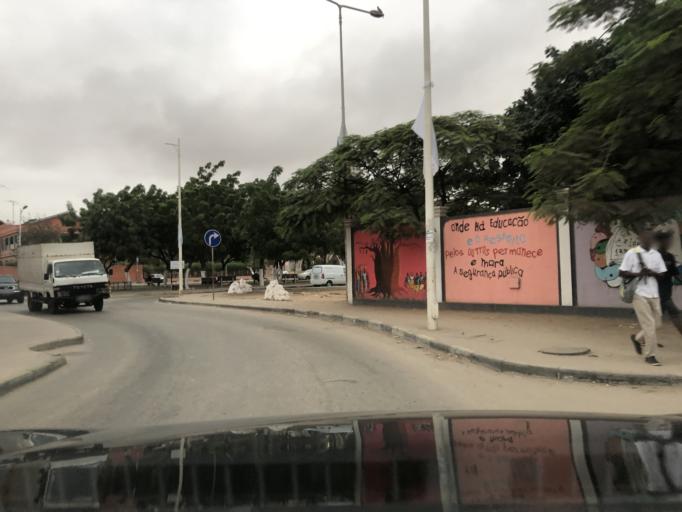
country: AO
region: Luanda
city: Luanda
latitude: -8.8293
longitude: 13.2566
